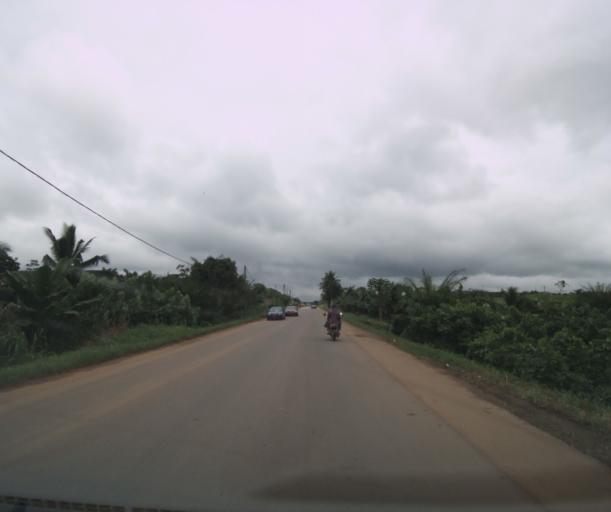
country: CM
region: Littoral
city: Edea
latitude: 3.7875
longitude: 10.1402
